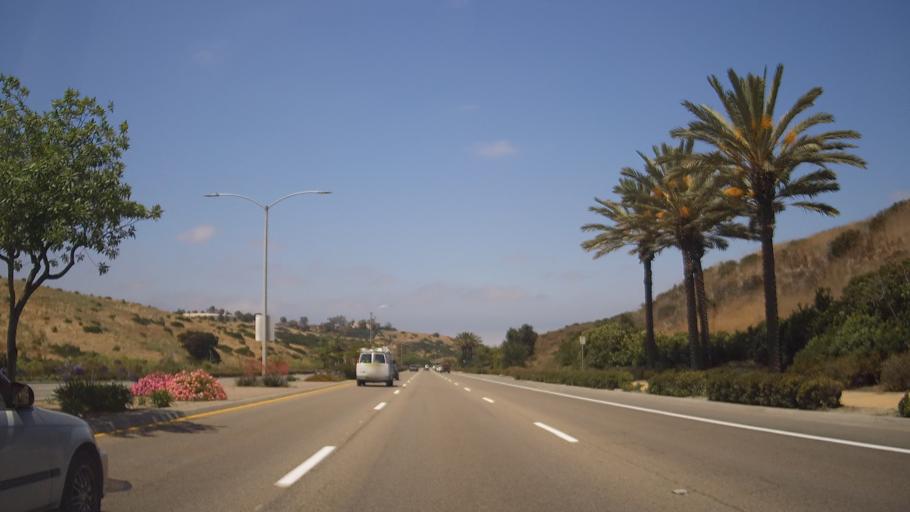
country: US
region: California
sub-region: San Diego County
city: Bonita
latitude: 32.6108
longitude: -117.0139
